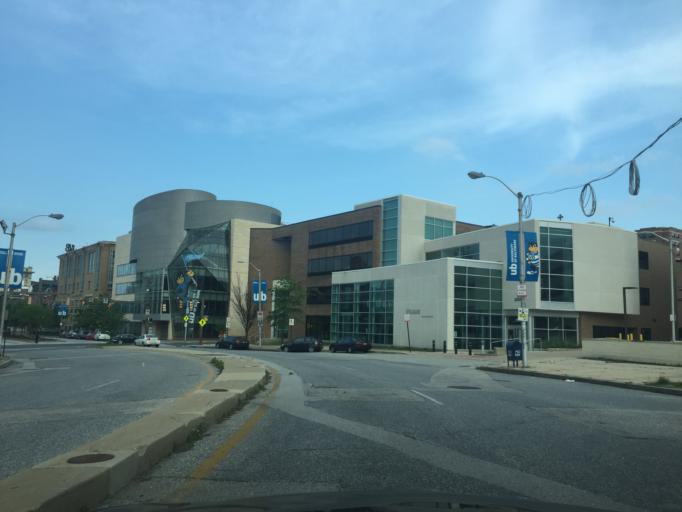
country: US
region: Maryland
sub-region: City of Baltimore
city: Baltimore
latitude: 39.3056
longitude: -76.6185
